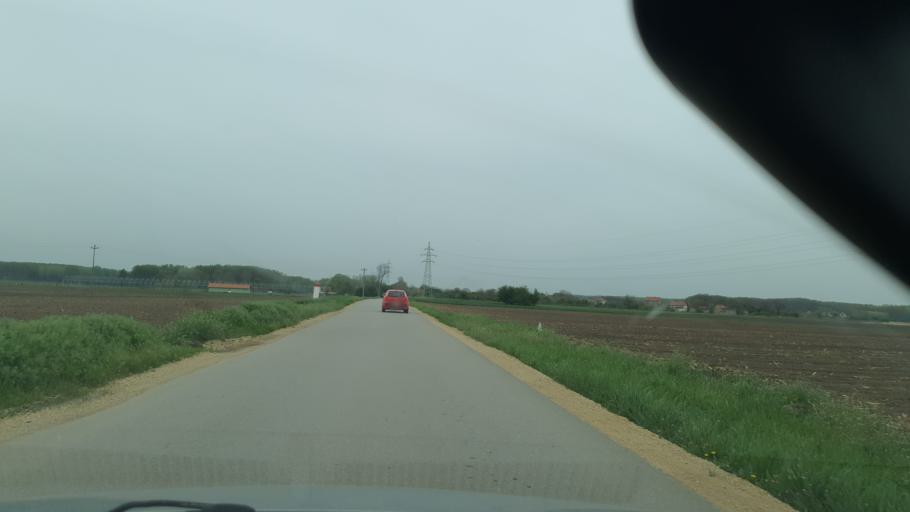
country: RS
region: Central Serbia
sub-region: Branicevski Okrug
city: Pozarevac
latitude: 44.7124
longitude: 21.1291
